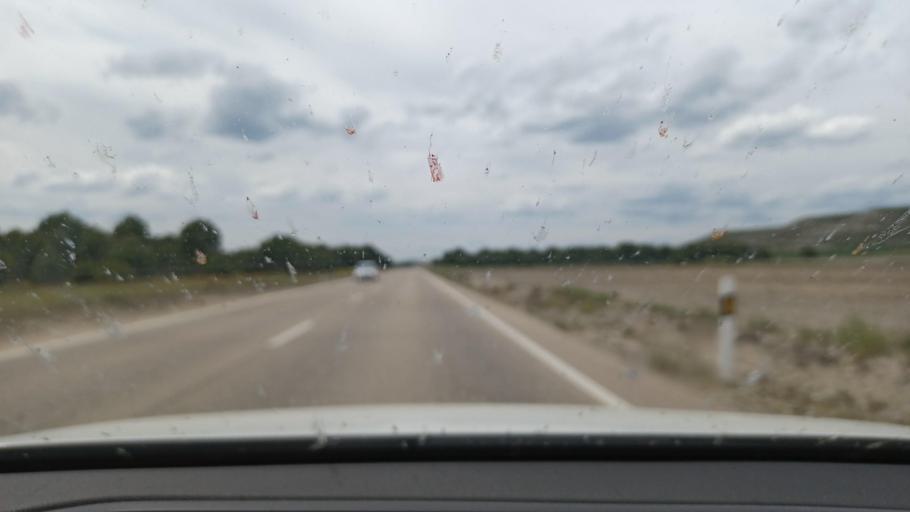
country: ES
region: Castille and Leon
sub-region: Provincia de Segovia
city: Frumales
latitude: 41.3827
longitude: -4.2212
